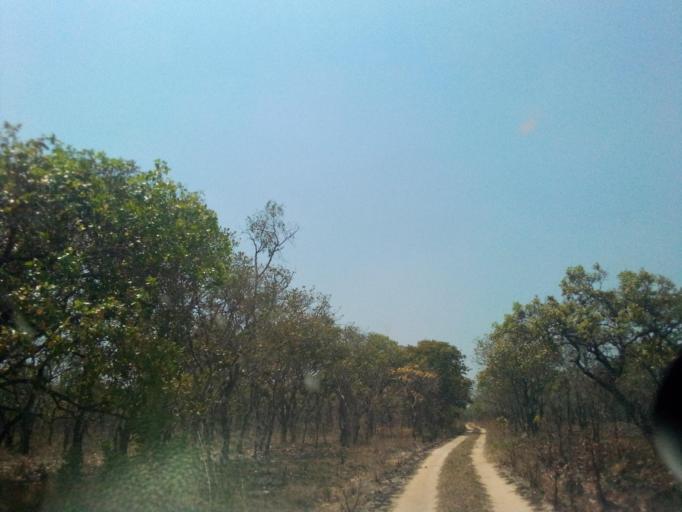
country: ZM
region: Copperbelt
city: Kataba
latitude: -12.2432
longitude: 30.3992
